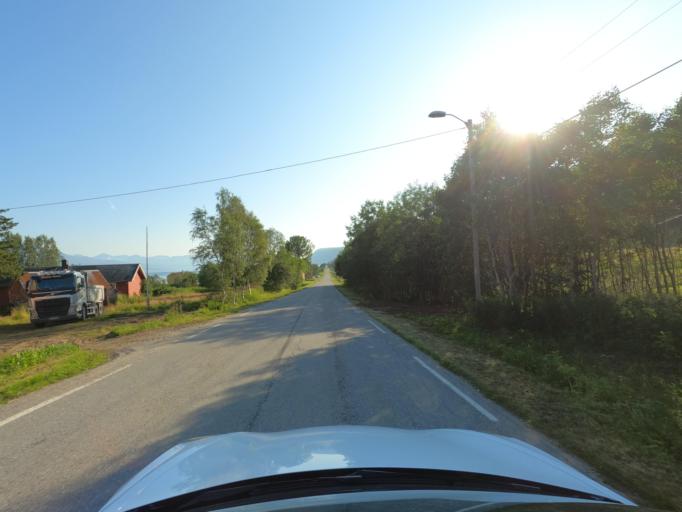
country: NO
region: Nordland
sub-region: Narvik
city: Bjerkvik
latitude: 68.5320
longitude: 17.4742
